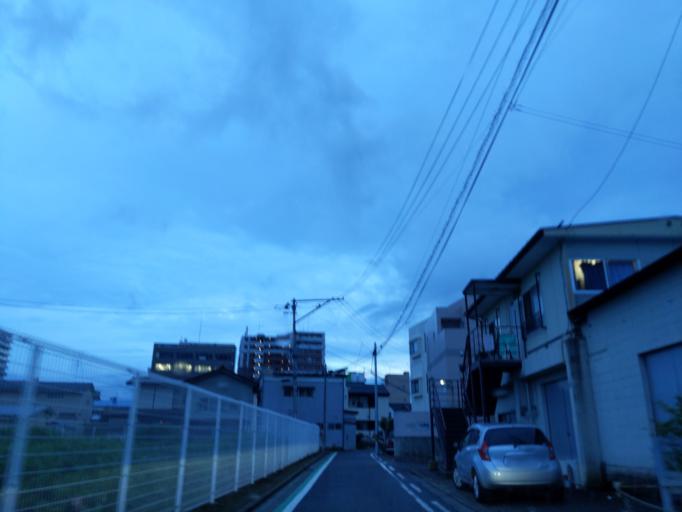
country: JP
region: Fukushima
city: Koriyama
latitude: 37.4009
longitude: 140.3658
